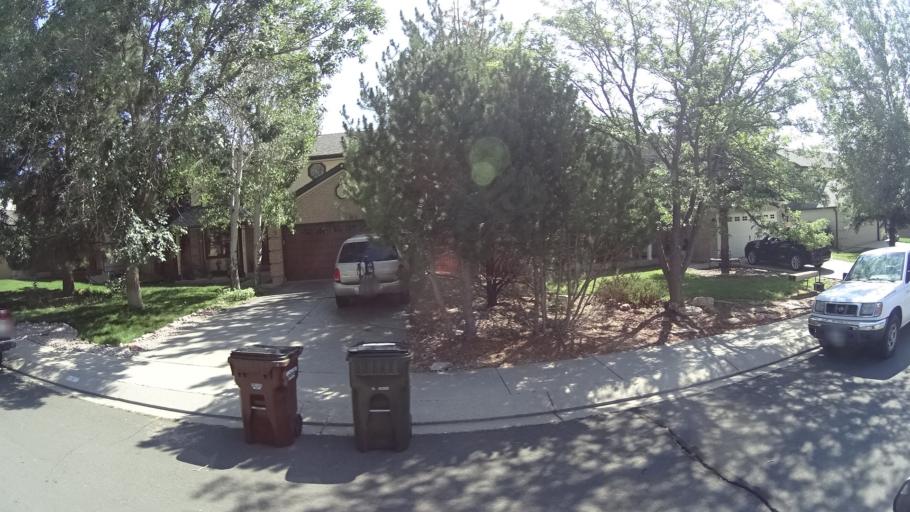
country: US
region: Colorado
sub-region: El Paso County
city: Air Force Academy
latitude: 38.9230
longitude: -104.8644
